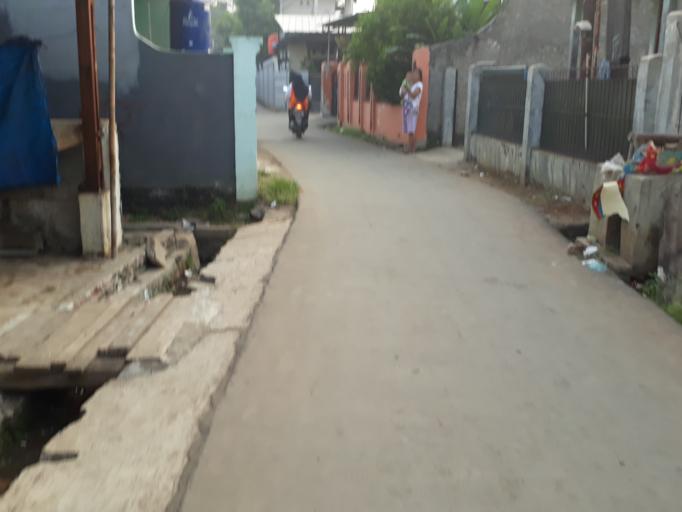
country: ID
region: West Java
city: Bekasi
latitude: -6.2474
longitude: 107.0683
